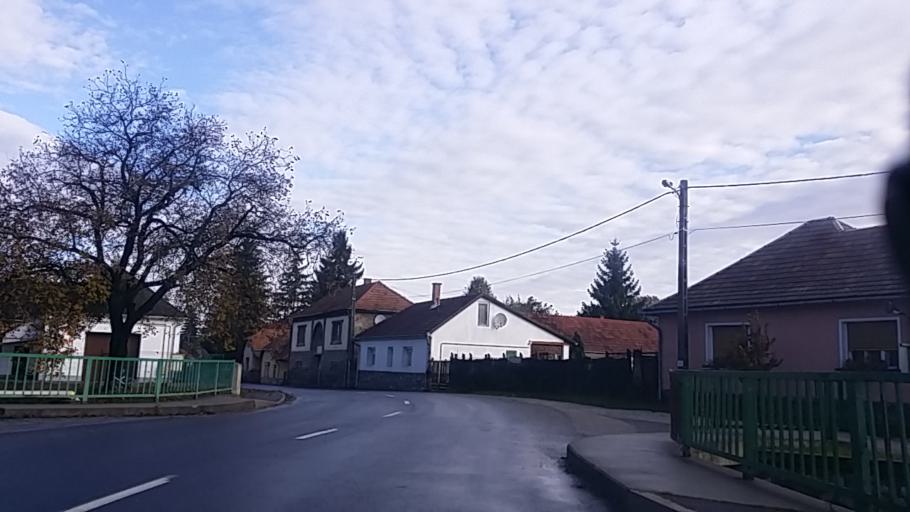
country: HU
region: Heves
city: Szilvasvarad
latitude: 48.1069
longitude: 20.3876
